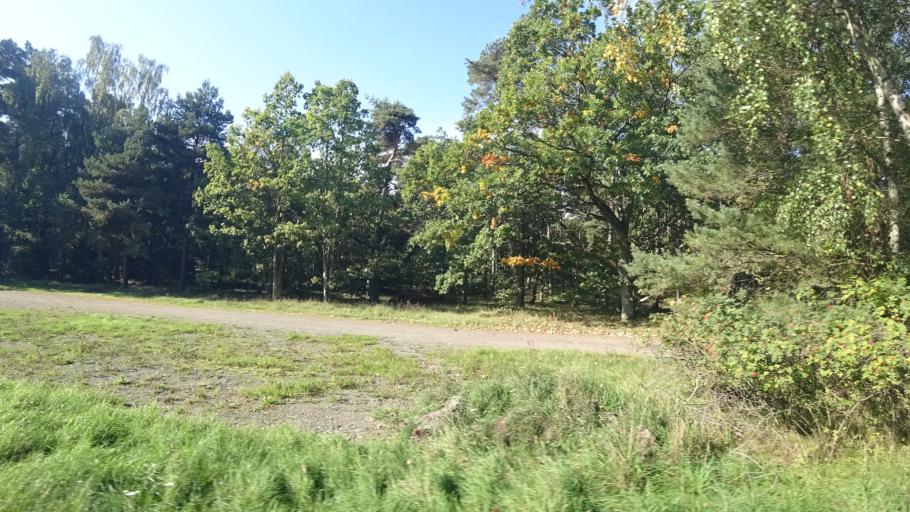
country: SE
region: Skane
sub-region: Kristianstads Kommun
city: Ahus
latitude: 55.9251
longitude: 14.3197
